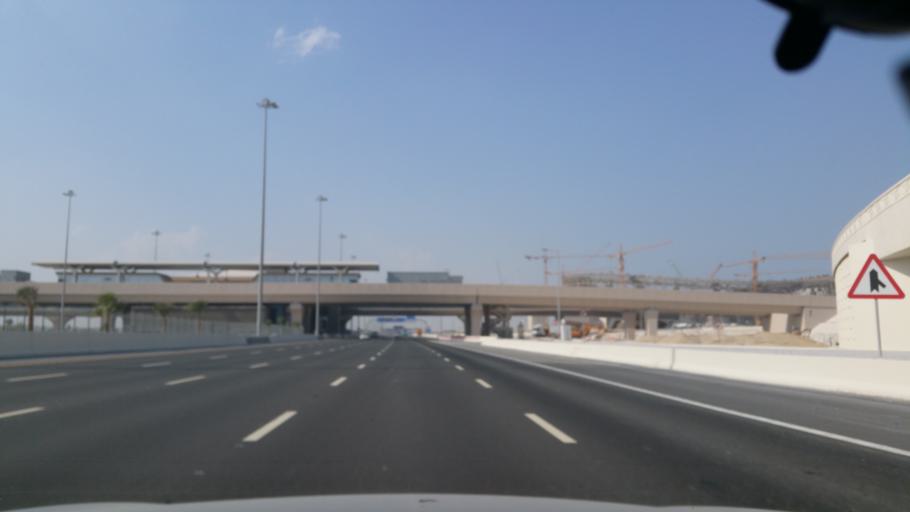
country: QA
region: Baladiyat Umm Salal
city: Umm Salal Muhammad
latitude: 25.4126
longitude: 51.4888
